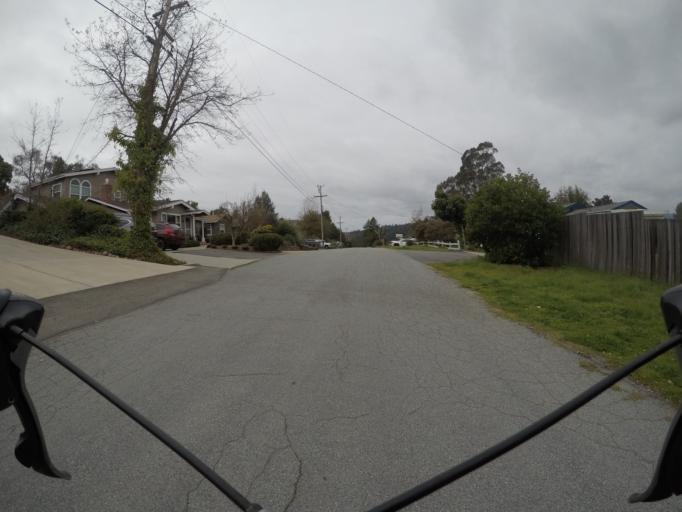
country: US
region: California
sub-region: Santa Cruz County
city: Scotts Valley
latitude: 37.0625
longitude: -121.9957
